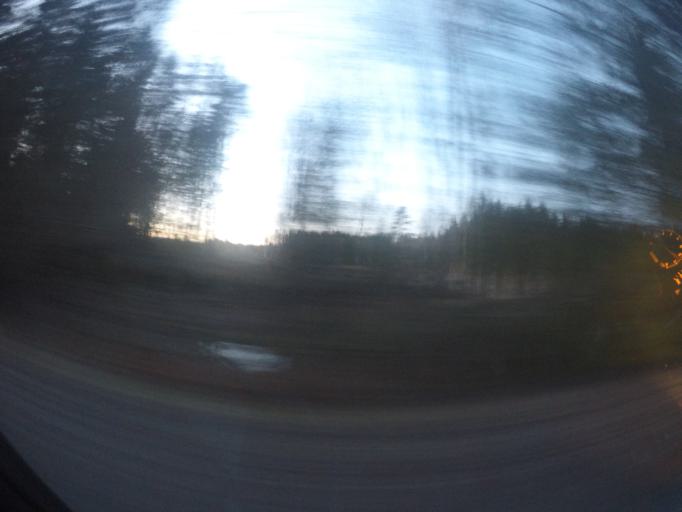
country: SE
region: OErebro
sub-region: Lindesbergs Kommun
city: Fellingsbro
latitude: 59.3539
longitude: 15.5770
